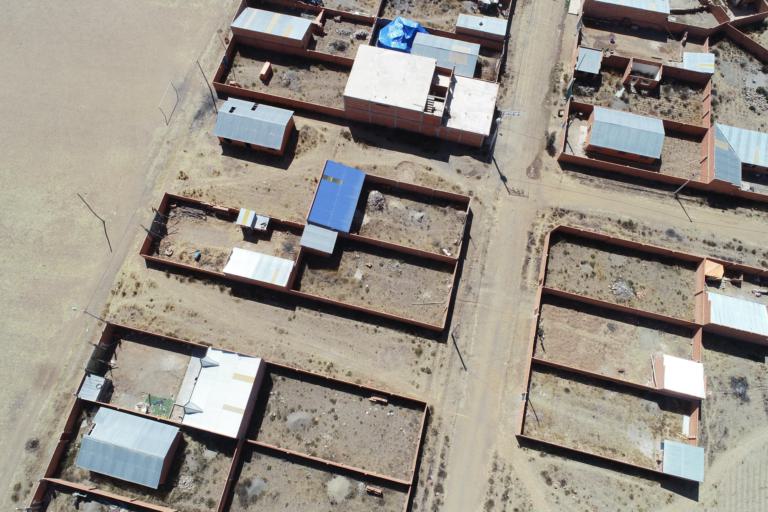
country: BO
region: La Paz
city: La Paz
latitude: -16.5948
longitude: -68.2121
